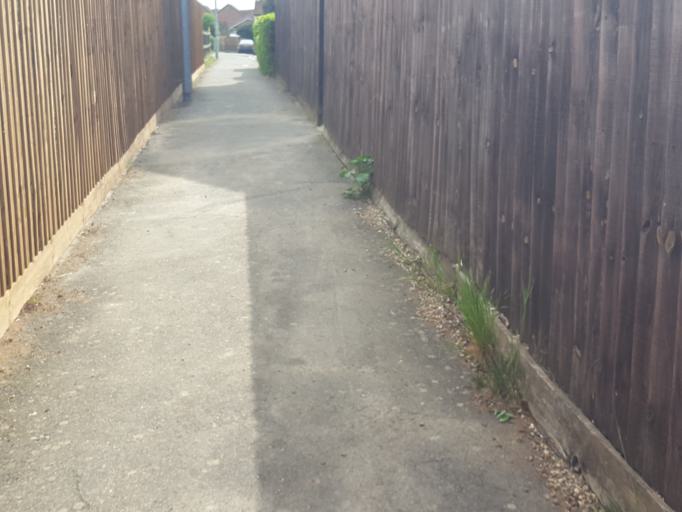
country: GB
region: England
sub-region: Essex
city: Frinton-on-Sea
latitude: 51.8435
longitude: 1.2153
